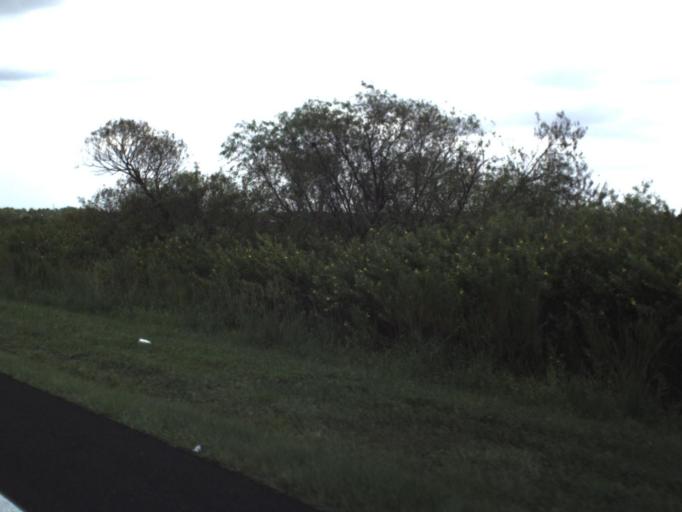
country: US
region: Florida
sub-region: Polk County
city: Dundee
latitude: 27.9787
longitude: -81.6375
